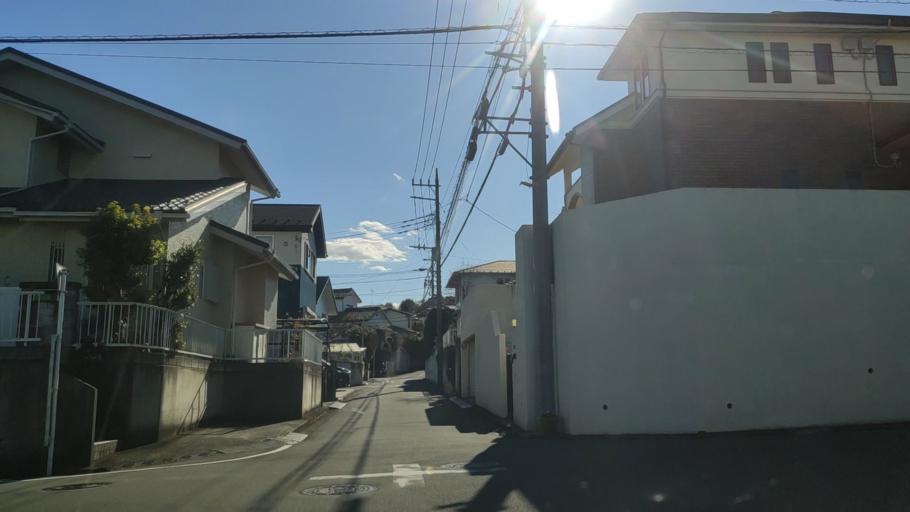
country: JP
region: Kanagawa
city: Minami-rinkan
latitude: 35.5075
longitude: 139.5253
